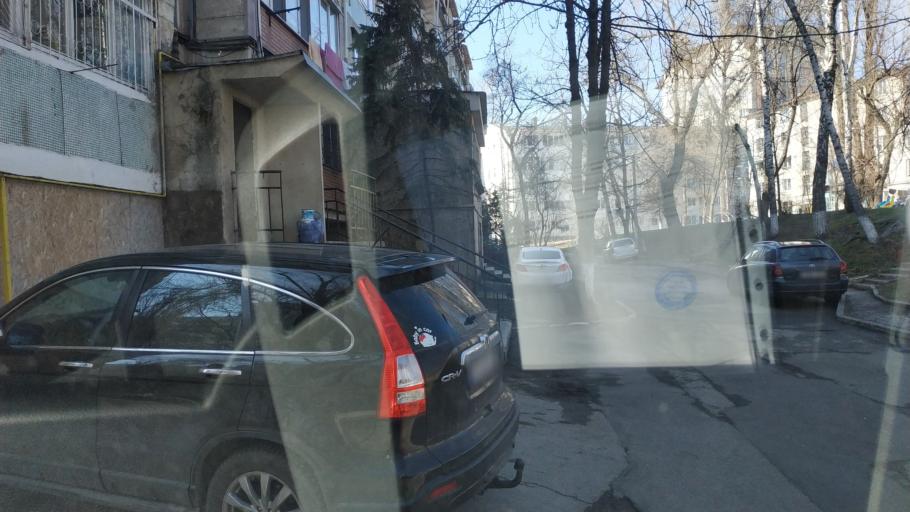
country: MD
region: Chisinau
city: Chisinau
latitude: 47.0289
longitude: 28.8012
